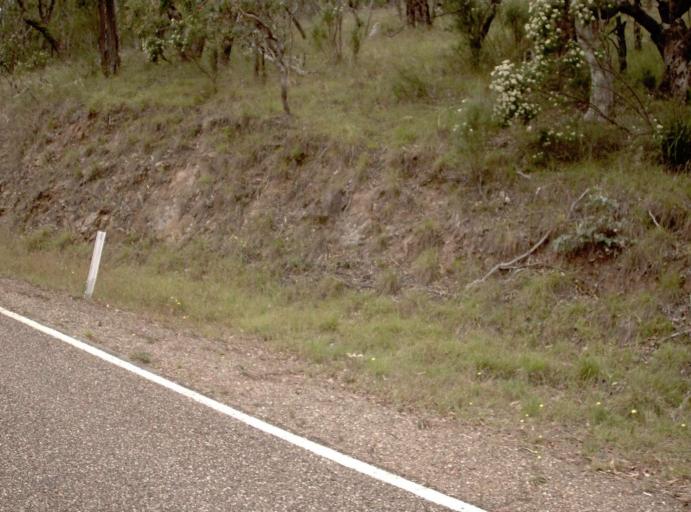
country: AU
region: Victoria
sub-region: East Gippsland
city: Bairnsdale
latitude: -37.5370
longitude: 147.2112
